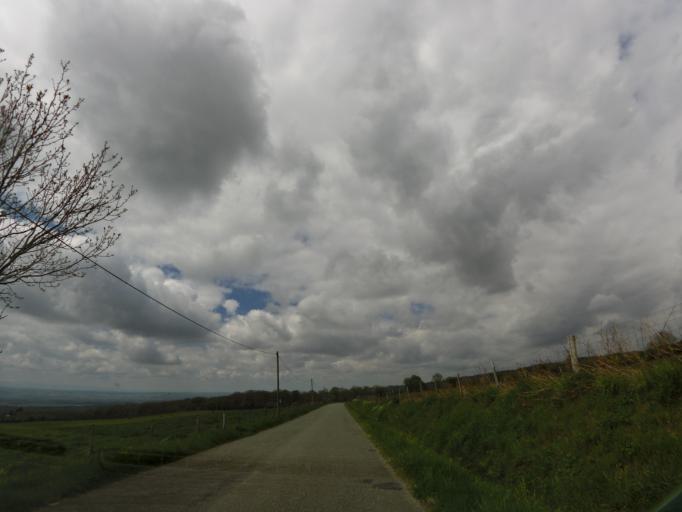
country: FR
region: Languedoc-Roussillon
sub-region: Departement de l'Aude
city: Villepinte
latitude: 43.3556
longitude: 2.1481
